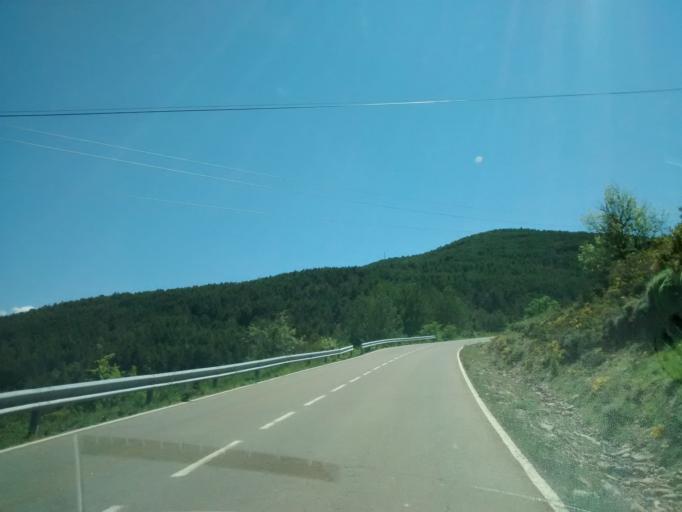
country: ES
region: Aragon
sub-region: Provincia de Huesca
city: Borau
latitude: 42.6545
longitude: -0.5668
